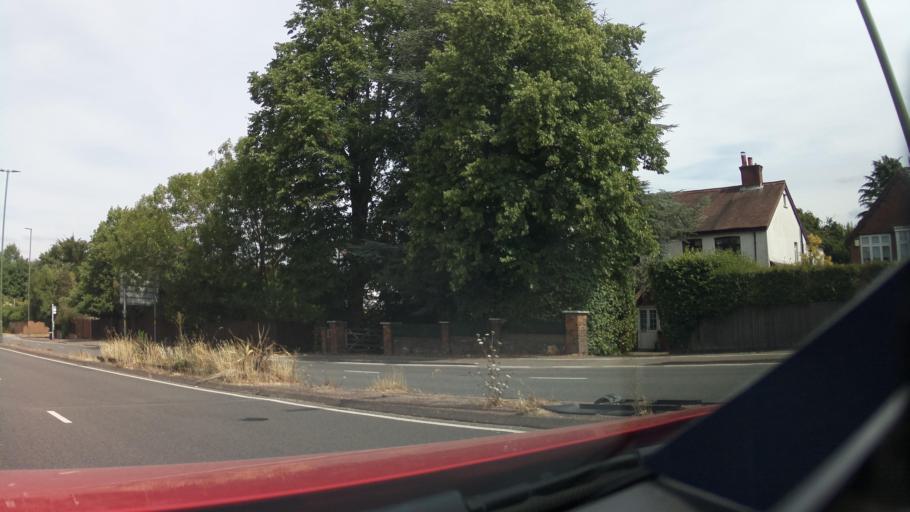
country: GB
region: England
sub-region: Surrey
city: Dorking
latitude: 51.2370
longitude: -0.3234
